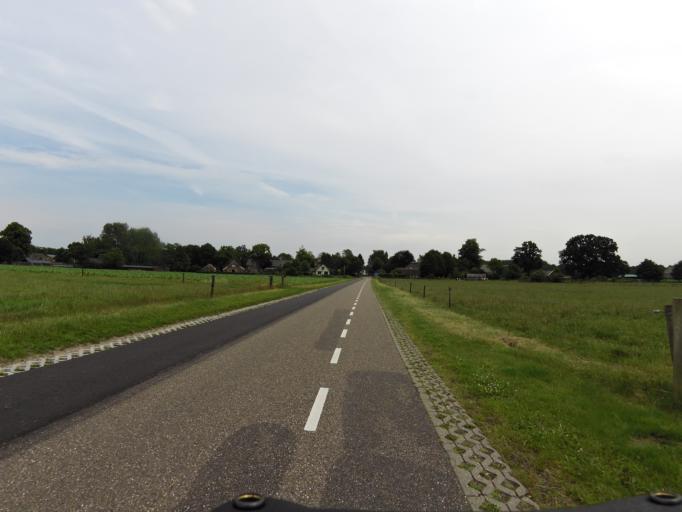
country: NL
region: Gelderland
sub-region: Gemeente Apeldoorn
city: Beekbergen
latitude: 52.1581
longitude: 6.0025
